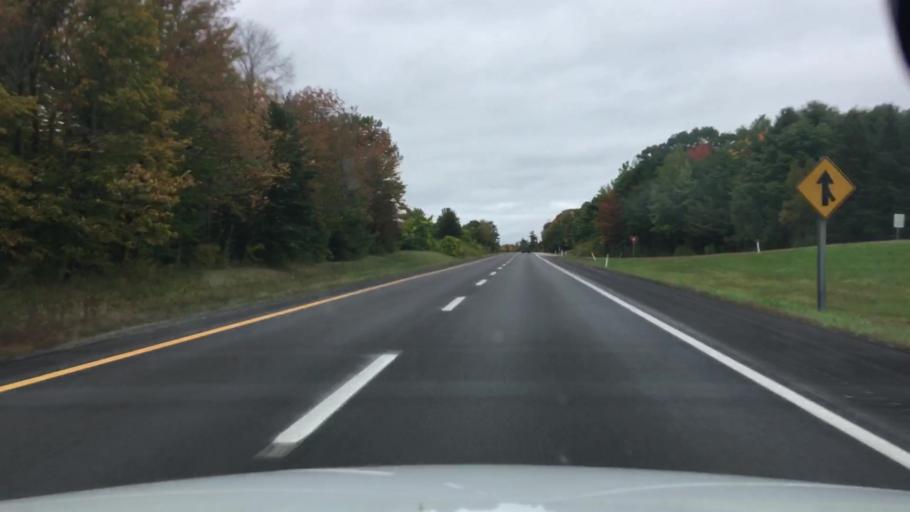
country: US
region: Maine
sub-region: Penobscot County
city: Orono
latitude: 44.8734
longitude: -68.7019
